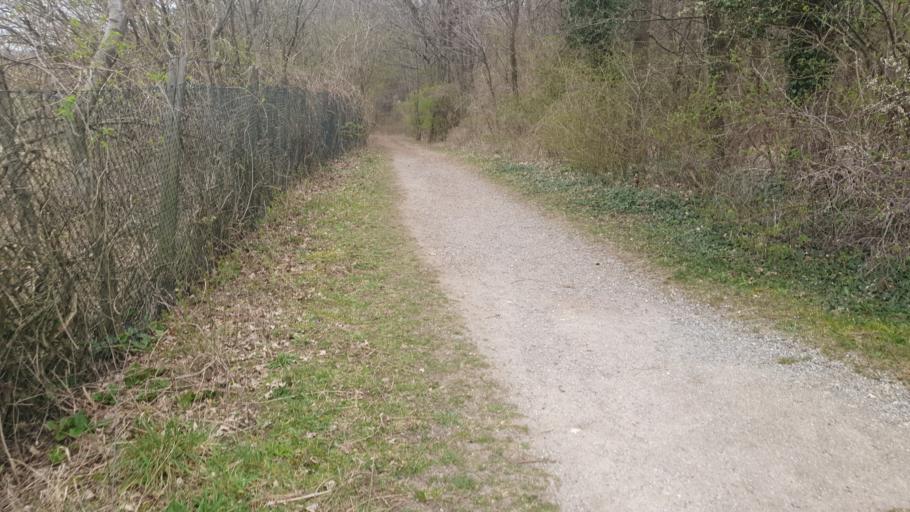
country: DE
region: North Rhine-Westphalia
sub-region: Regierungsbezirk Munster
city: Rheine
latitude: 52.2573
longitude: 7.4395
